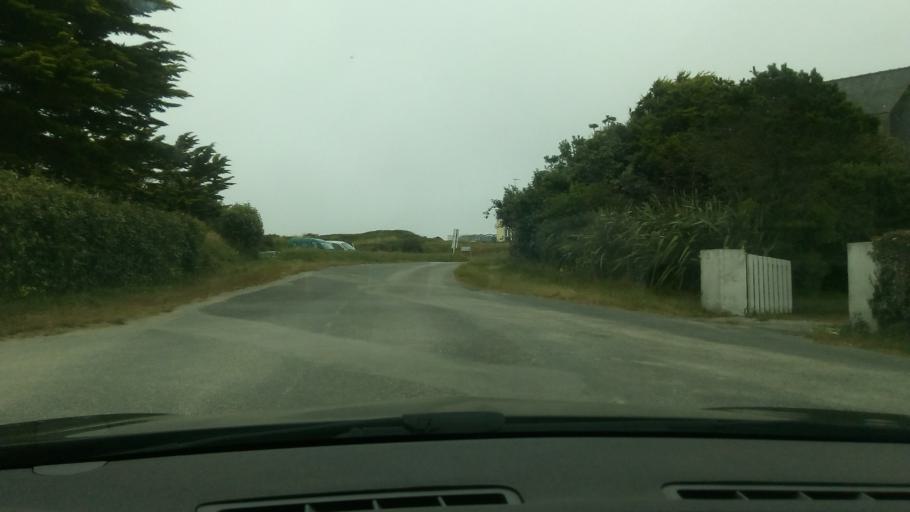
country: FR
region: Brittany
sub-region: Departement du Finistere
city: Le Conquet
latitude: 48.3649
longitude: -4.7670
